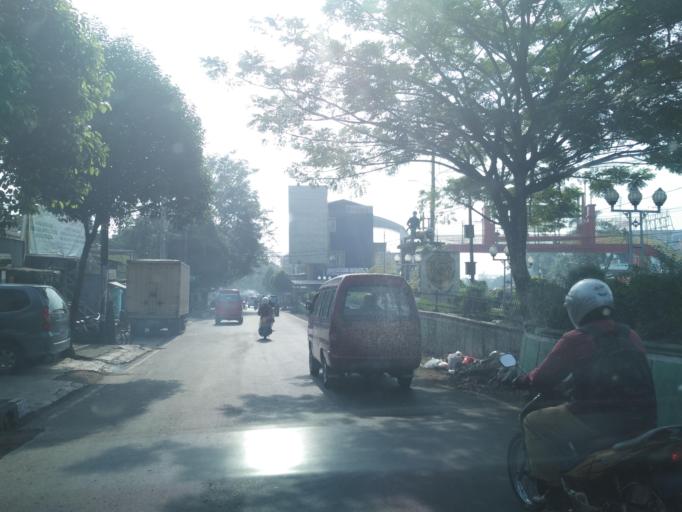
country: ID
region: West Java
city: Ciranjang-hilir
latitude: -6.8108
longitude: 107.1464
